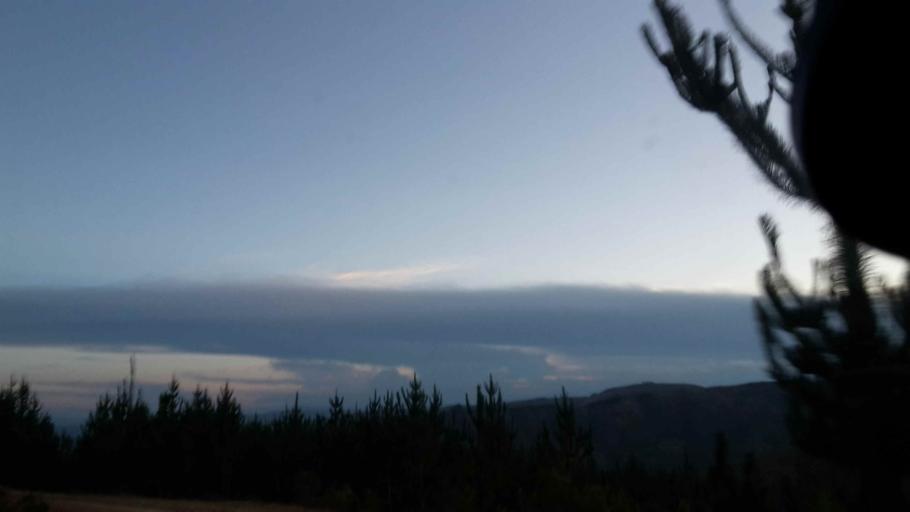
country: BO
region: Cochabamba
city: Mizque
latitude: -17.9134
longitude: -65.5057
